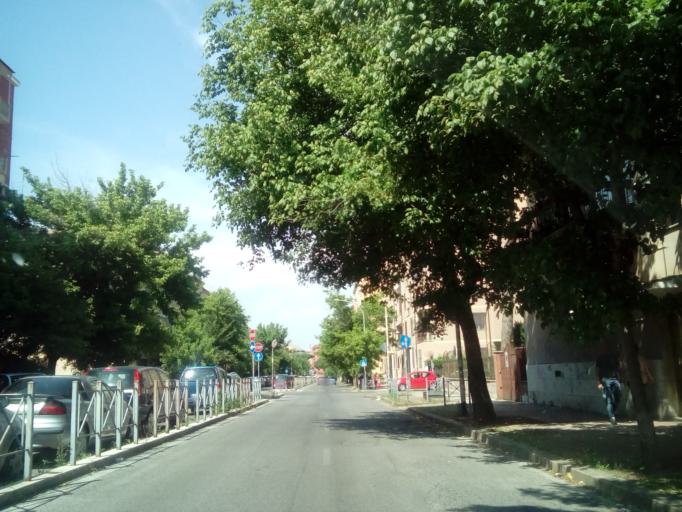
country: IT
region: Latium
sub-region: Citta metropolitana di Roma Capitale
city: Rome
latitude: 41.8564
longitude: 12.5538
